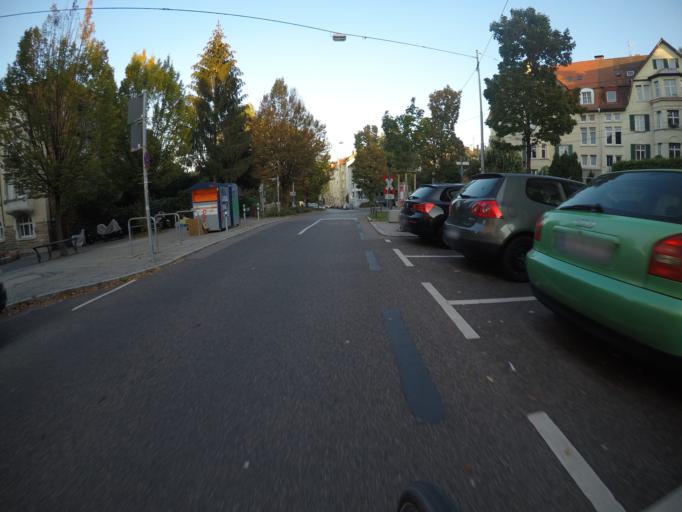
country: DE
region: Baden-Wuerttemberg
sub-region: Regierungsbezirk Stuttgart
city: Stuttgart
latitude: 48.7629
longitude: 9.1689
